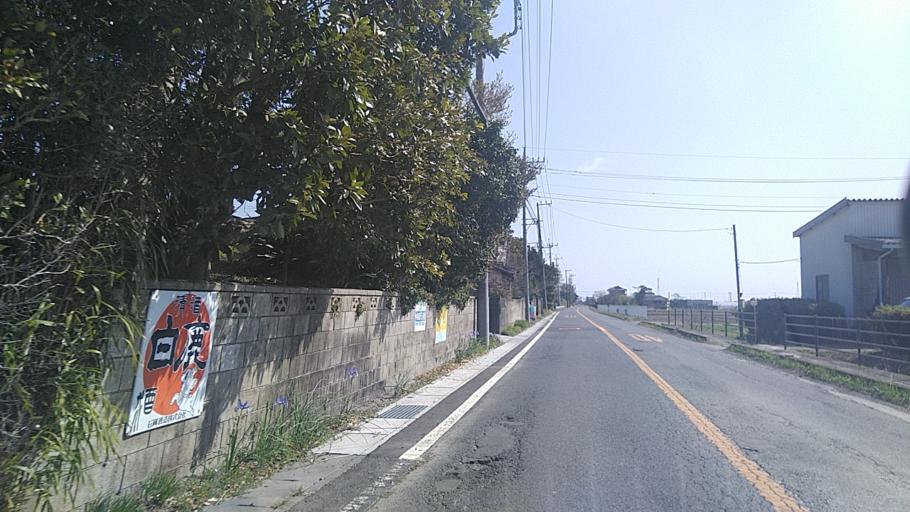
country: JP
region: Ibaraki
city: Ryugasaki
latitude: 35.8617
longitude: 140.1677
